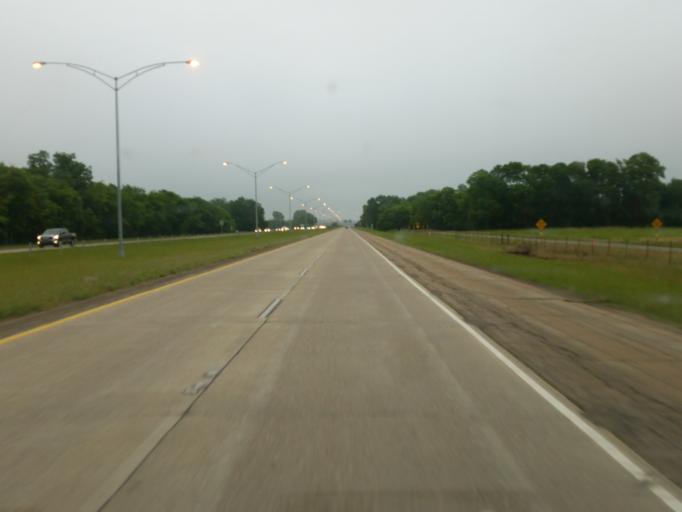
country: US
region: Louisiana
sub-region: Bossier Parish
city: Red Chute
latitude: 32.5350
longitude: -93.6484
